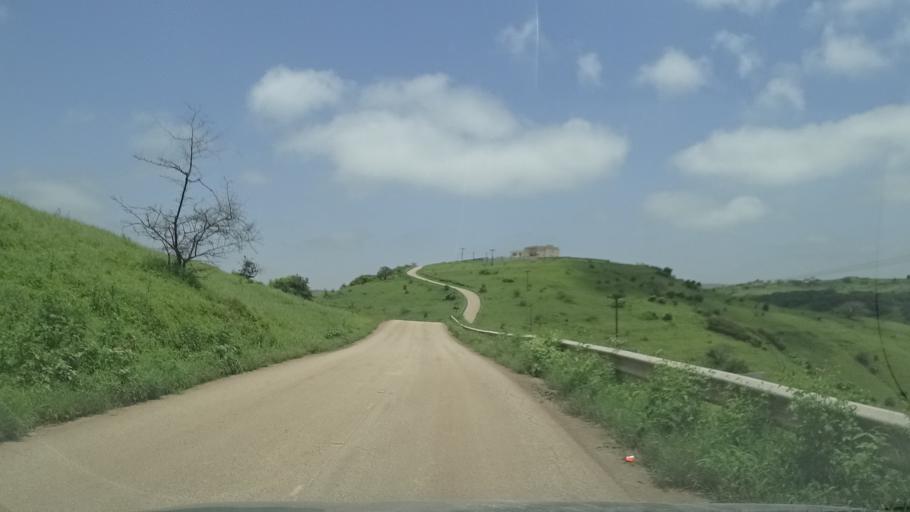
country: OM
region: Zufar
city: Salalah
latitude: 17.2173
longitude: 54.2013
